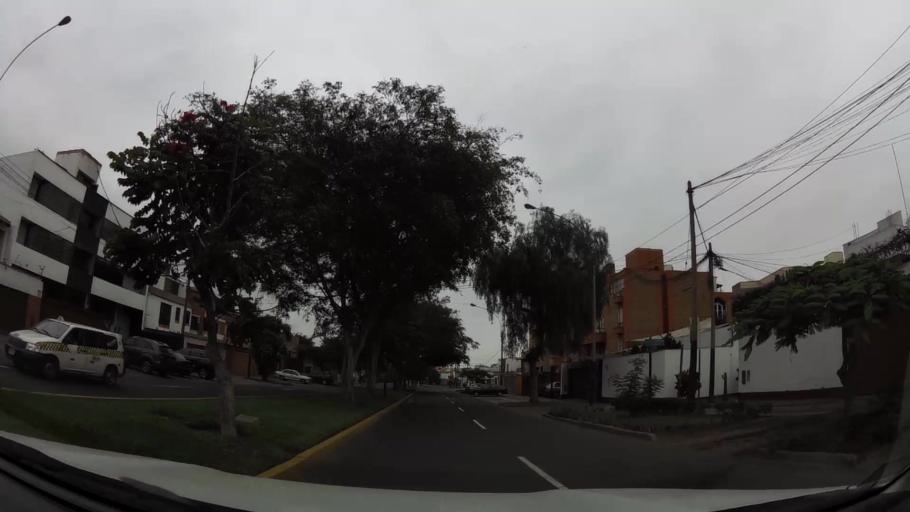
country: PE
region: Lima
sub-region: Lima
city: La Molina
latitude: -12.1118
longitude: -76.9736
